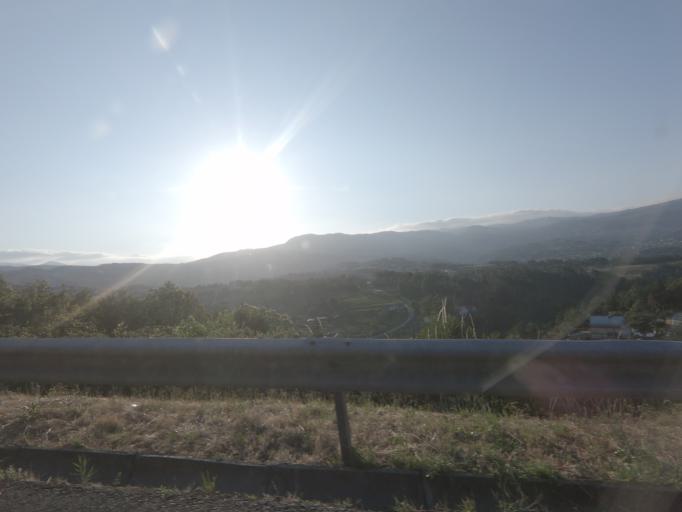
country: PT
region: Vila Real
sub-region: Vila Real
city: Vila Real
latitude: 41.2795
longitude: -7.7687
